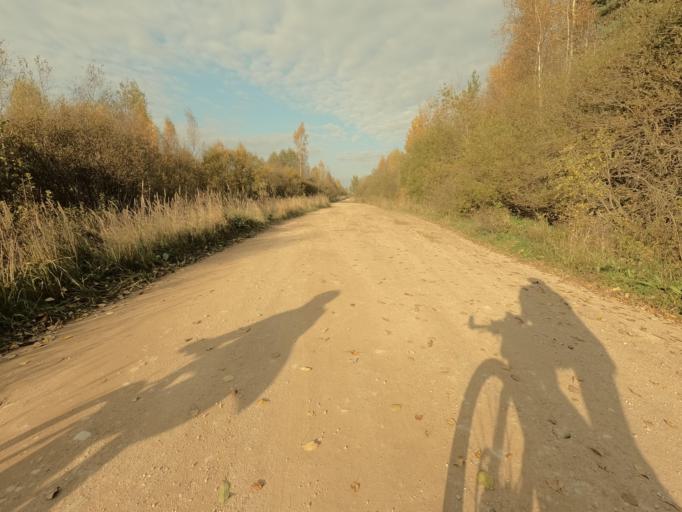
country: RU
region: Novgorod
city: Volkhovskiy
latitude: 58.9023
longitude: 31.0342
